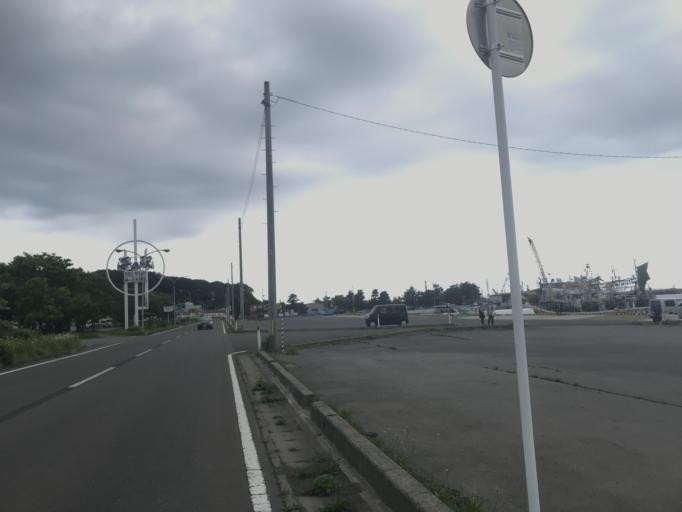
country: JP
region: Aomori
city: Shimokizukuri
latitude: 40.7792
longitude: 140.2123
